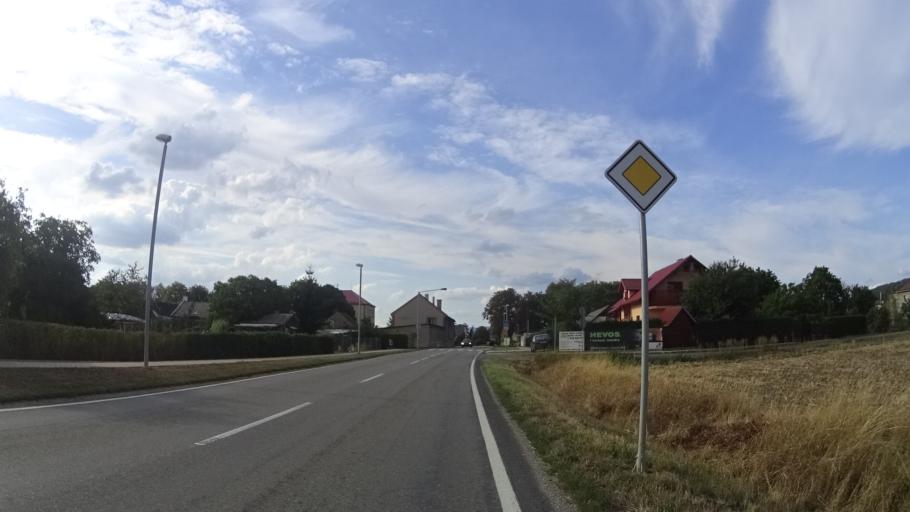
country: CZ
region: Olomoucky
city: Lestina
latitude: 49.8684
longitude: 16.9337
